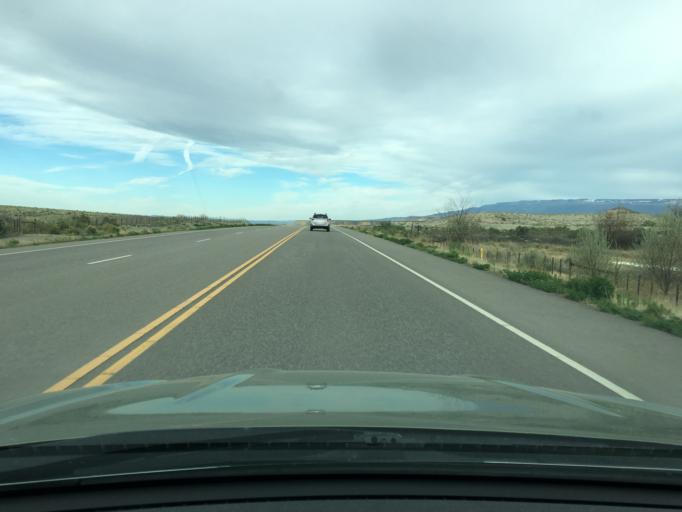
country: US
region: Colorado
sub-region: Delta County
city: Orchard City
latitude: 38.8027
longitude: -107.8790
